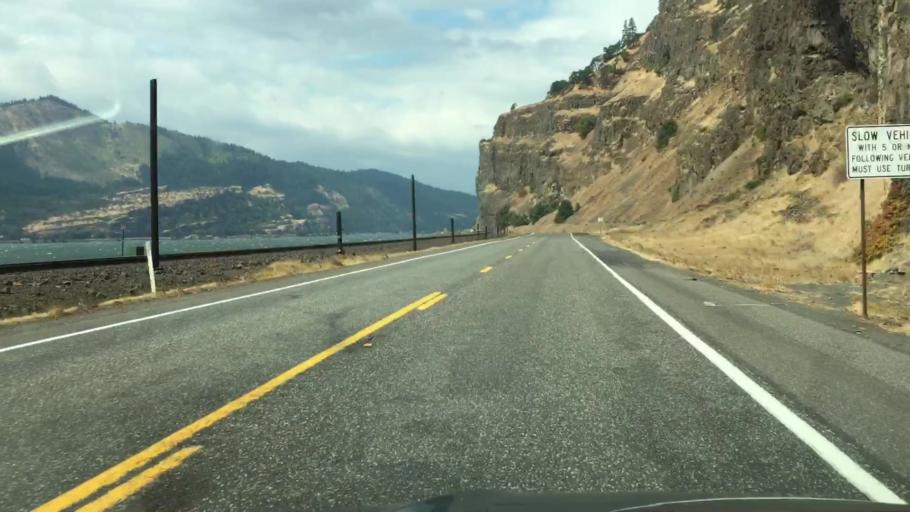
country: US
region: Washington
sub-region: Klickitat County
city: White Salmon
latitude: 45.6991
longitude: -121.4111
